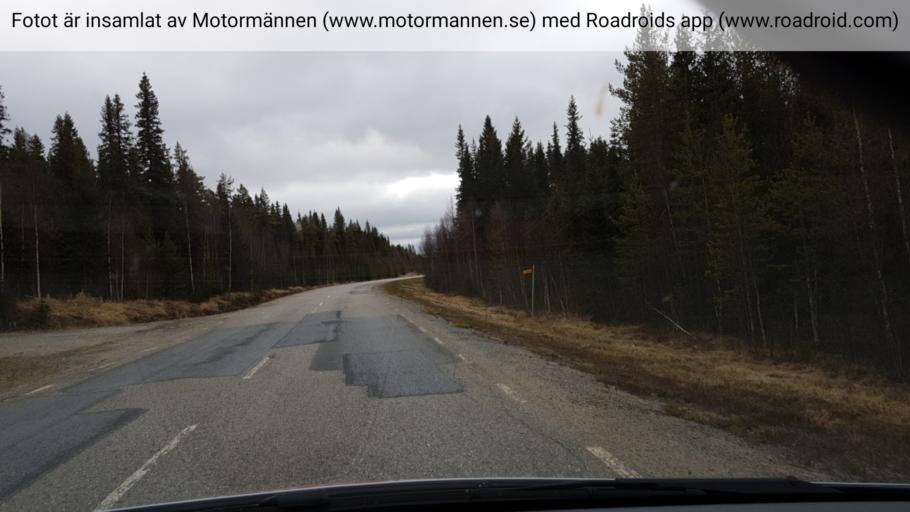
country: SE
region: Vaesterbotten
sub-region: Lycksele Kommun
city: Lycksele
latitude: 64.0078
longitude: 18.4613
